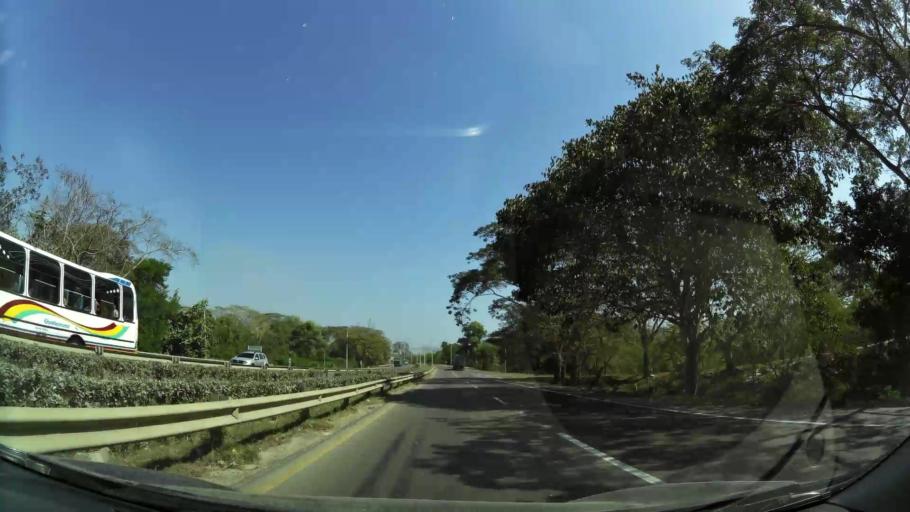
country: CO
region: Bolivar
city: Turbaco
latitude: 10.3719
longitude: -75.4532
